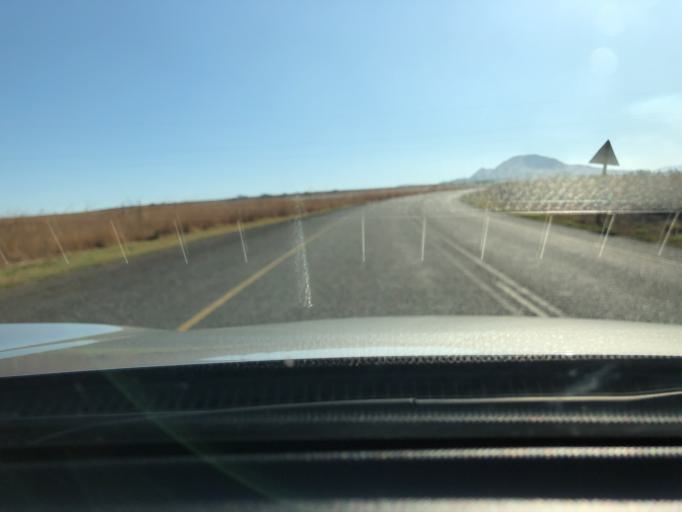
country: ZA
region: KwaZulu-Natal
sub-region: uThukela District Municipality
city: Ekuvukeni
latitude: -28.4067
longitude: 29.9534
